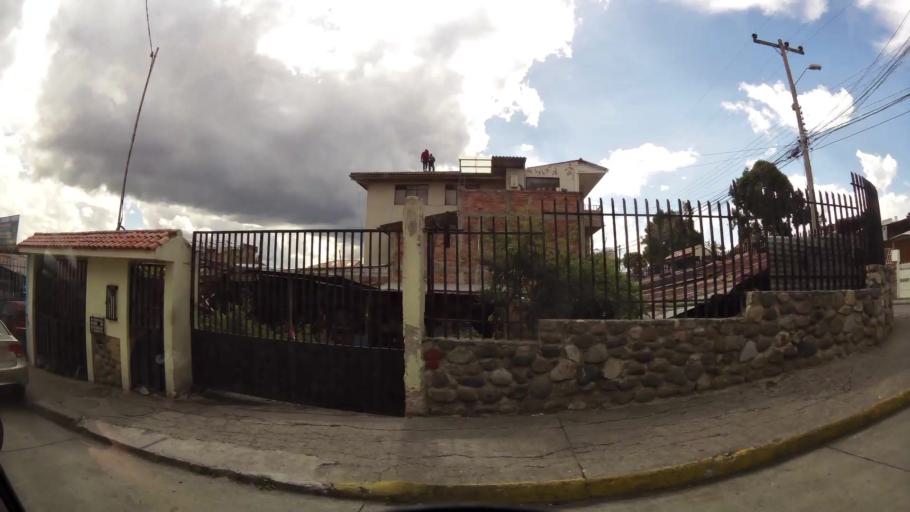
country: EC
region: Azuay
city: Cuenca
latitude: -2.8890
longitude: -78.9963
